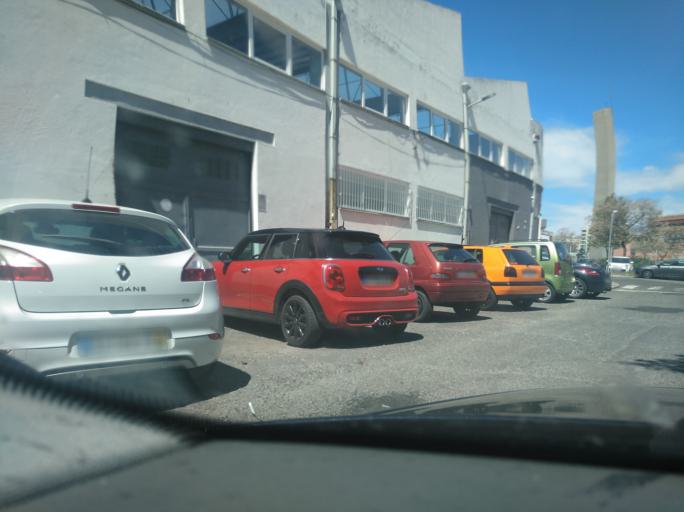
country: PT
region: Lisbon
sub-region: Amadora
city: Amadora
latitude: 38.7376
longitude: -9.2165
